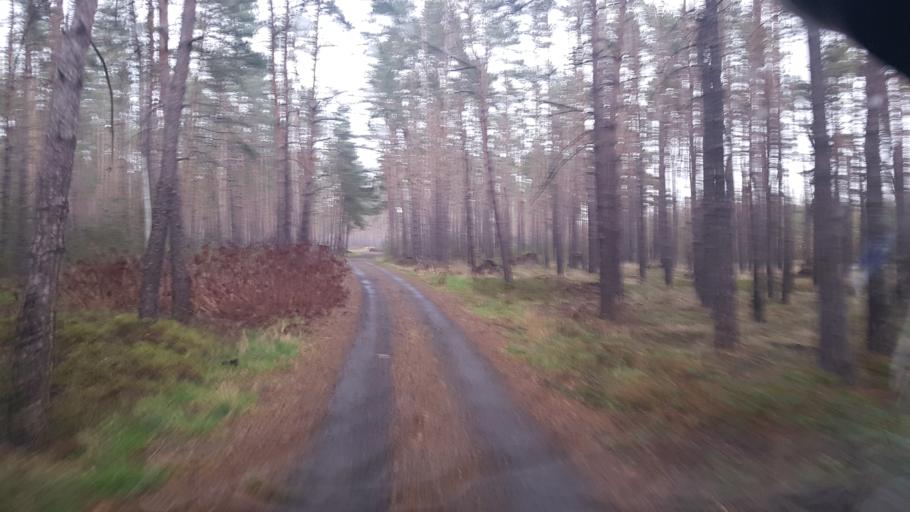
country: DE
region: Brandenburg
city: Muhlberg
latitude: 51.4963
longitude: 13.2974
